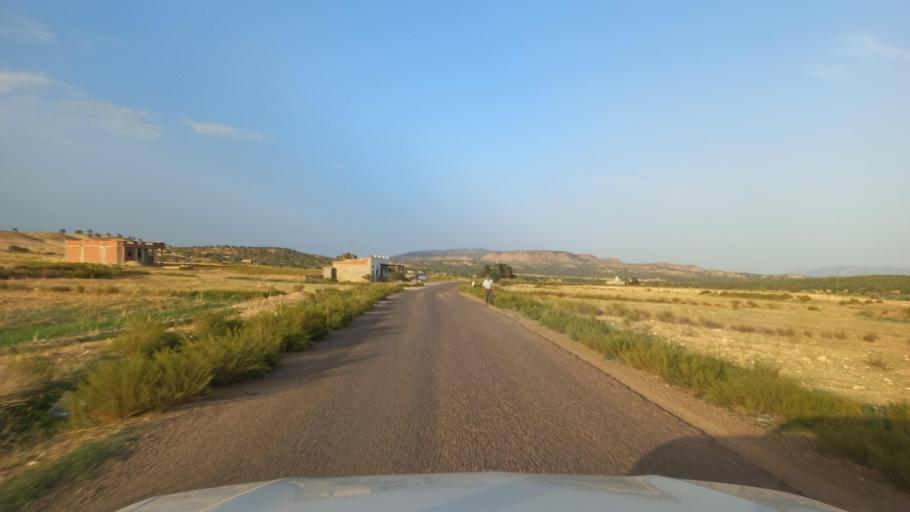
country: TN
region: Al Qasrayn
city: Sbiba
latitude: 35.4047
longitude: 8.9009
